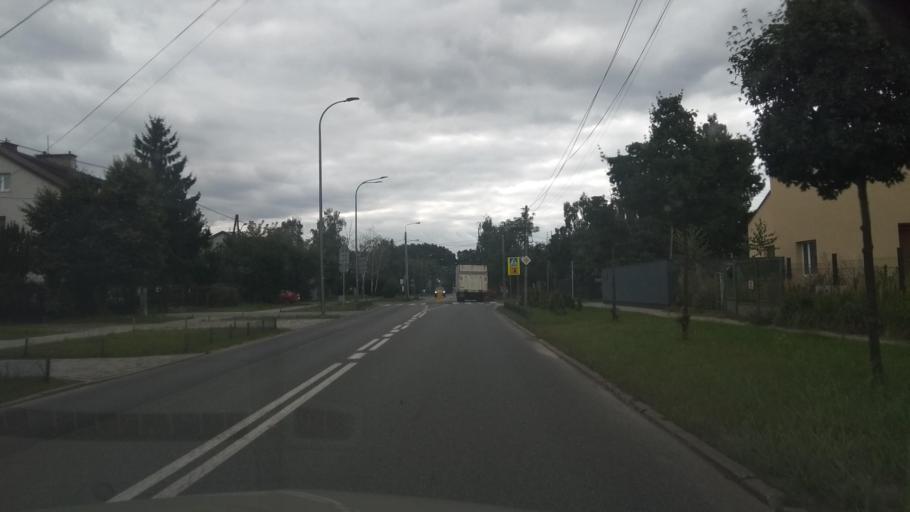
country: PL
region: Masovian Voivodeship
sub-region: Warszawa
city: Wawer
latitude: 52.2141
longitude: 21.1458
